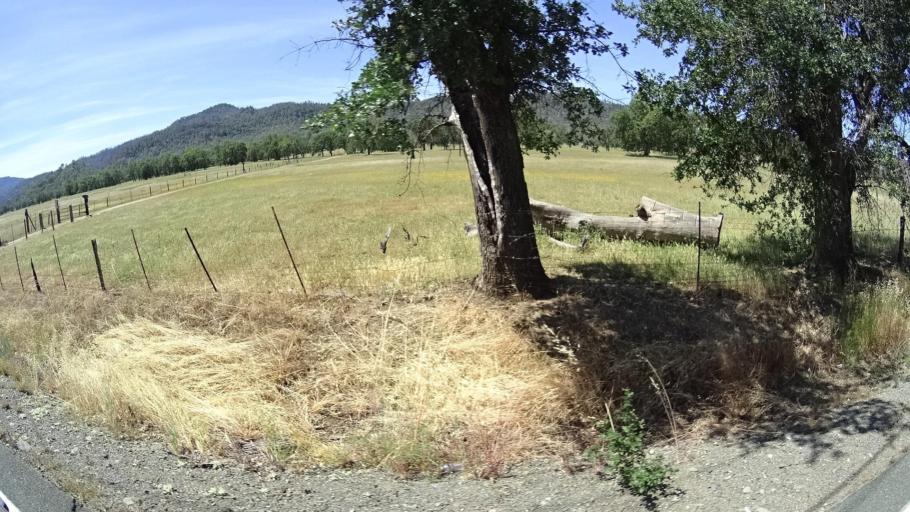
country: US
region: California
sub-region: Lake County
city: Middletown
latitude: 38.7393
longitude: -122.5684
